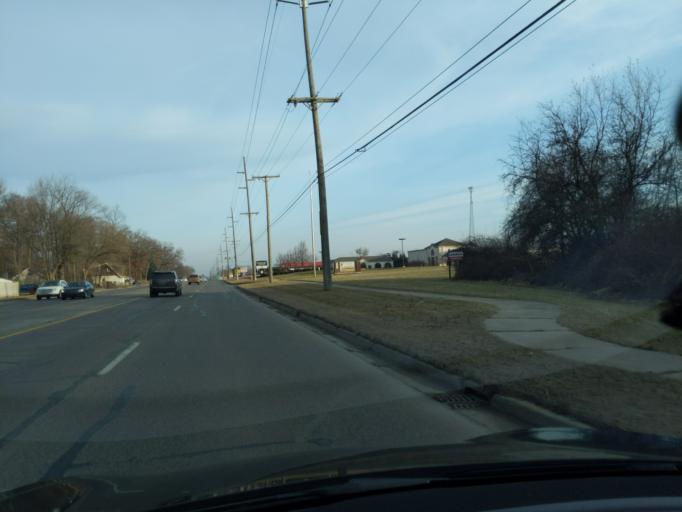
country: US
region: Michigan
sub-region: Livingston County
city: Brighton
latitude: 42.5760
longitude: -83.8406
